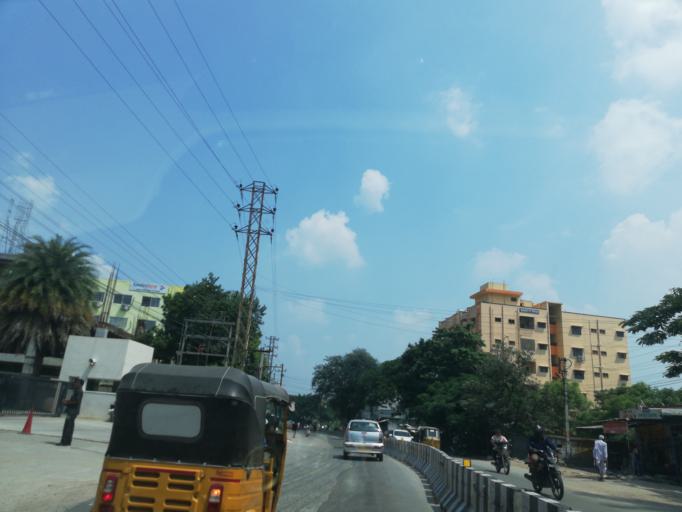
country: IN
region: Telangana
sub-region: Medak
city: Serilingampalle
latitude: 17.4825
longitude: 78.3204
